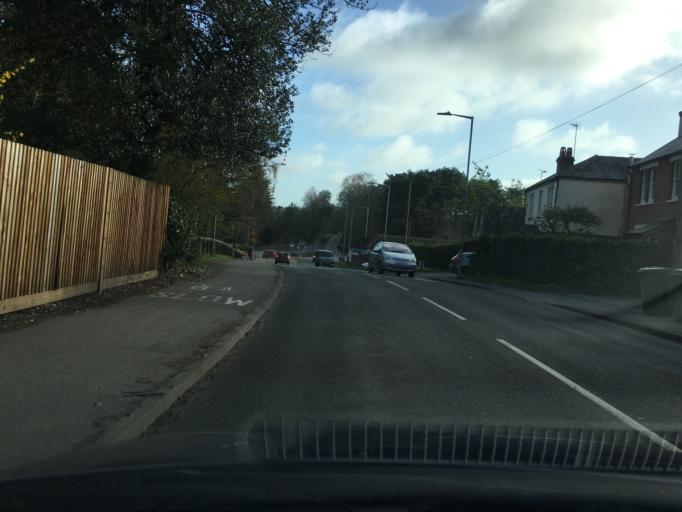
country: GB
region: England
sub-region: Bracknell Forest
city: Crowthorne
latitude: 51.3711
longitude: -0.7898
